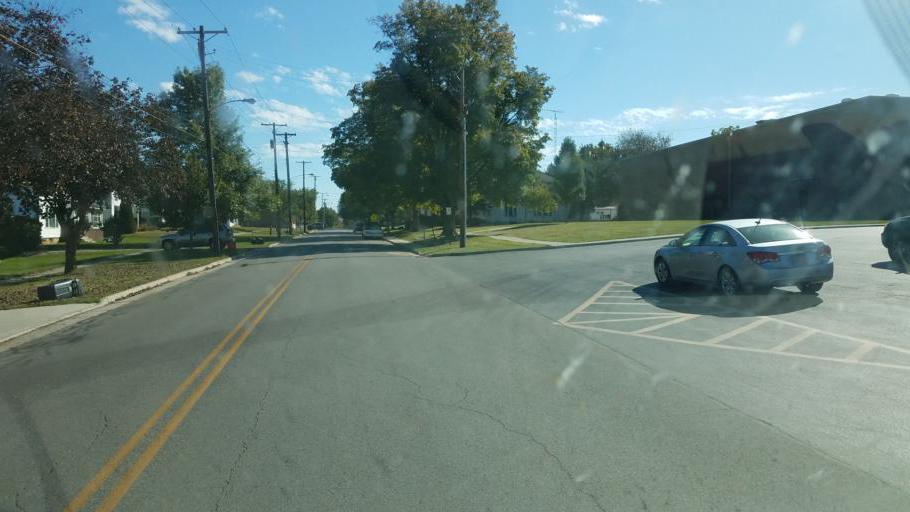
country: US
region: Ohio
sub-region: Wyandot County
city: Upper Sandusky
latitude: 40.8303
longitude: -83.2879
